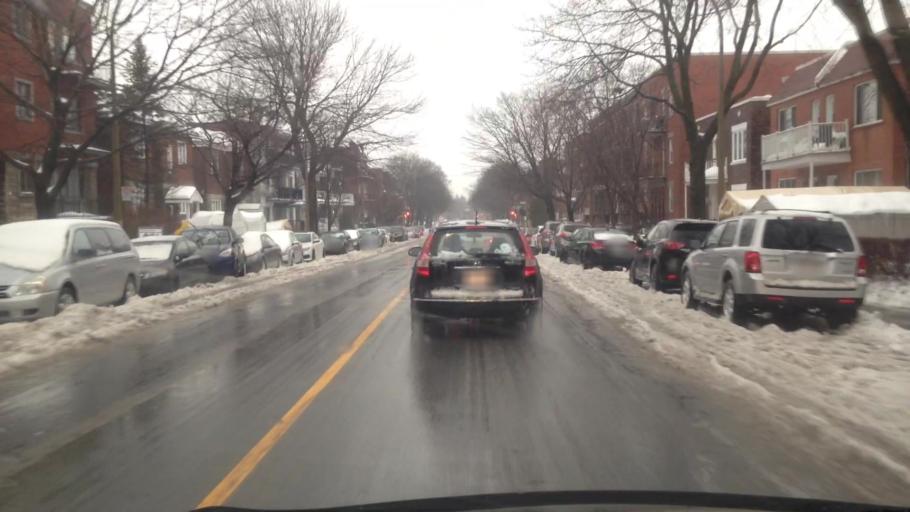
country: CA
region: Quebec
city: Mont-Royal
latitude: 45.5040
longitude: -73.6295
